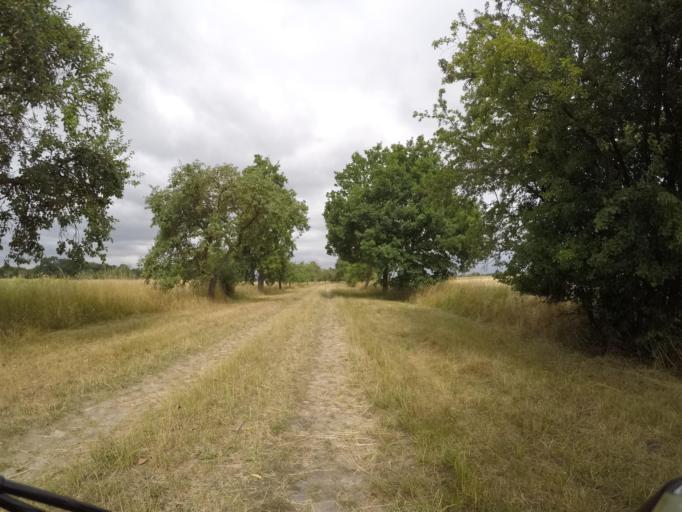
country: DE
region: Lower Saxony
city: Hitzacker
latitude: 53.1704
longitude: 11.0419
